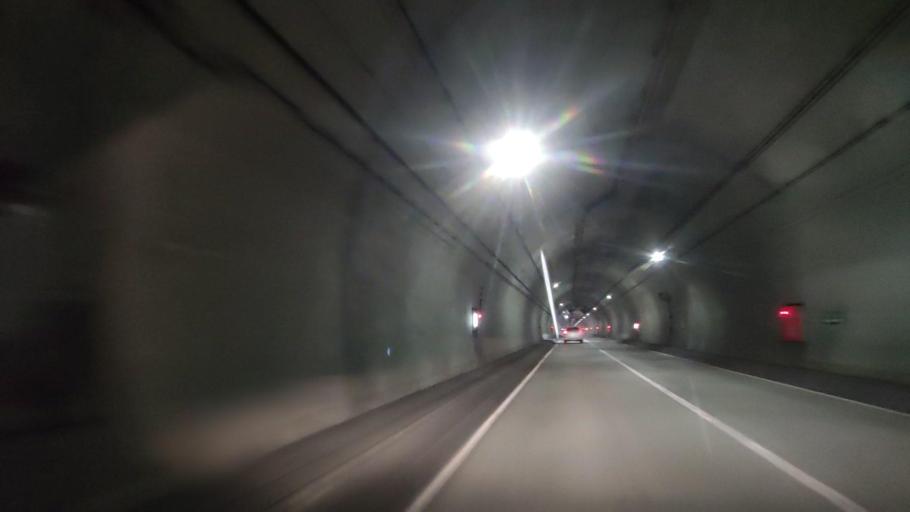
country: JP
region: Hokkaido
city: Rumoi
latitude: 43.7220
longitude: 141.3303
